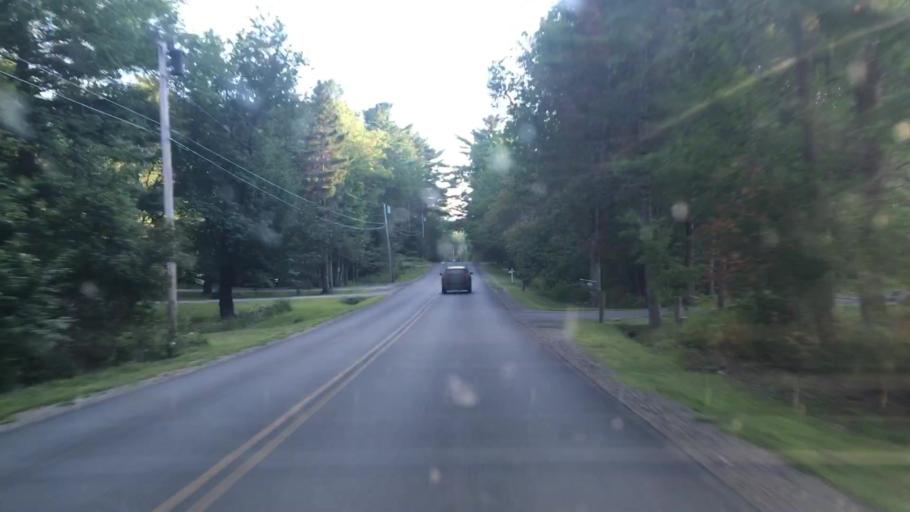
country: US
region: Maine
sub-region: Waldo County
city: Winterport
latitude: 44.6940
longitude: -68.9004
